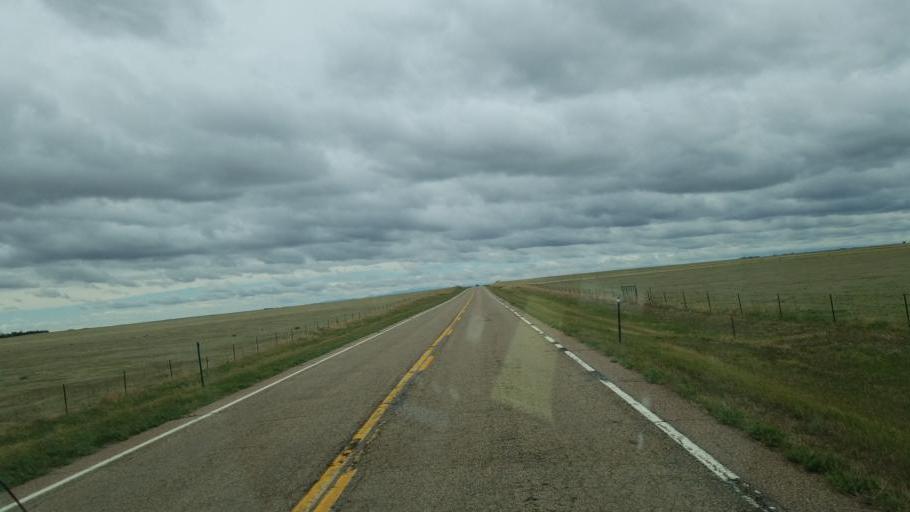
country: US
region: Colorado
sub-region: El Paso County
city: Ellicott
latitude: 38.8395
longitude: -103.9128
